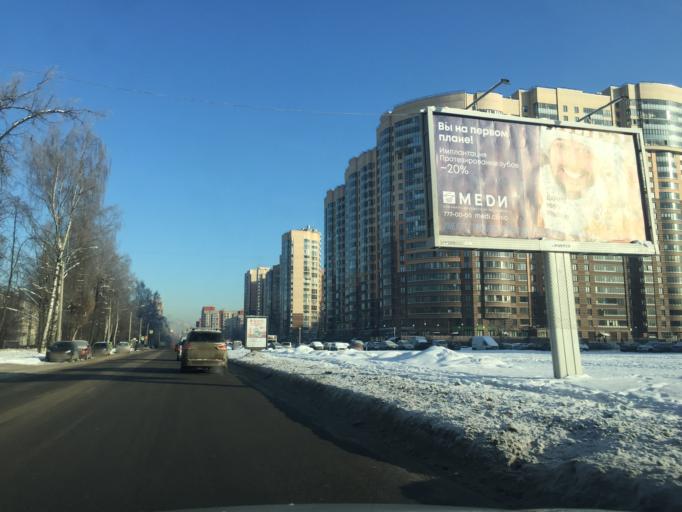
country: RU
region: Leningrad
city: Kalininskiy
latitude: 60.0020
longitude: 30.3969
